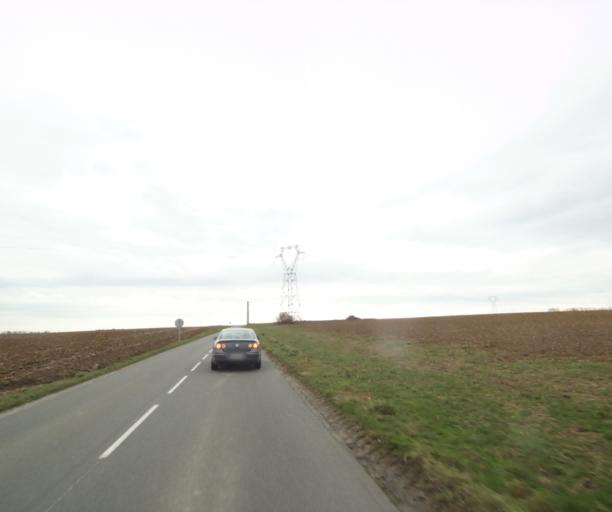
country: FR
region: Nord-Pas-de-Calais
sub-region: Departement du Nord
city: Curgies
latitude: 50.3542
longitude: 3.6119
